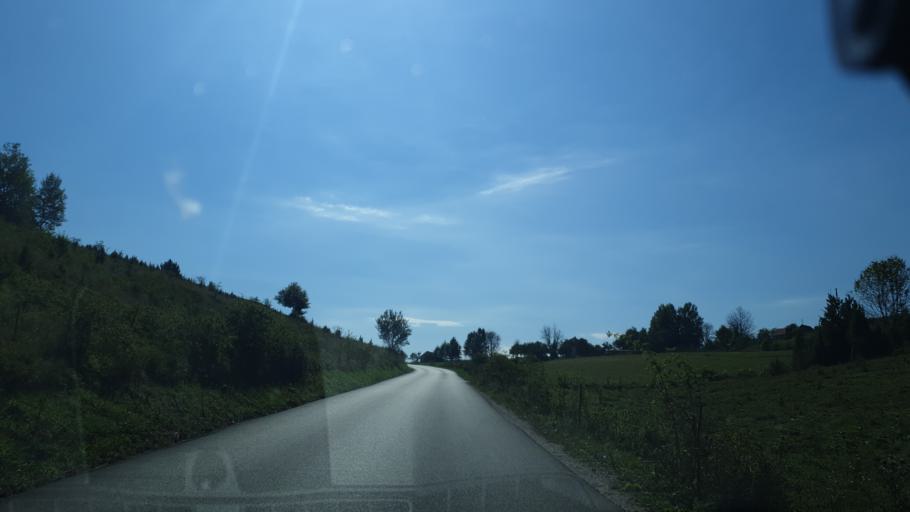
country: RS
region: Central Serbia
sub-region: Zlatiborski Okrug
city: Nova Varos
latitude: 43.4287
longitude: 19.8736
